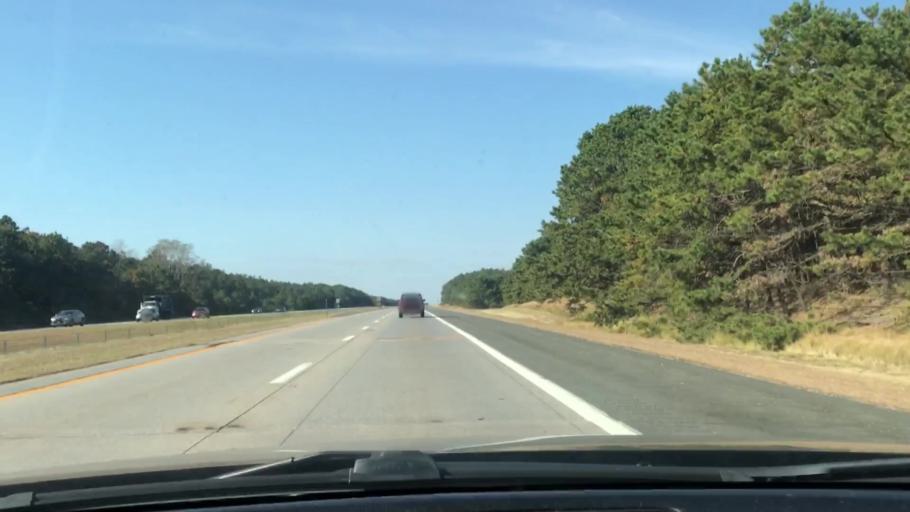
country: US
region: New York
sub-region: Suffolk County
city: East Quogue
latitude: 40.8755
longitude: -72.5685
